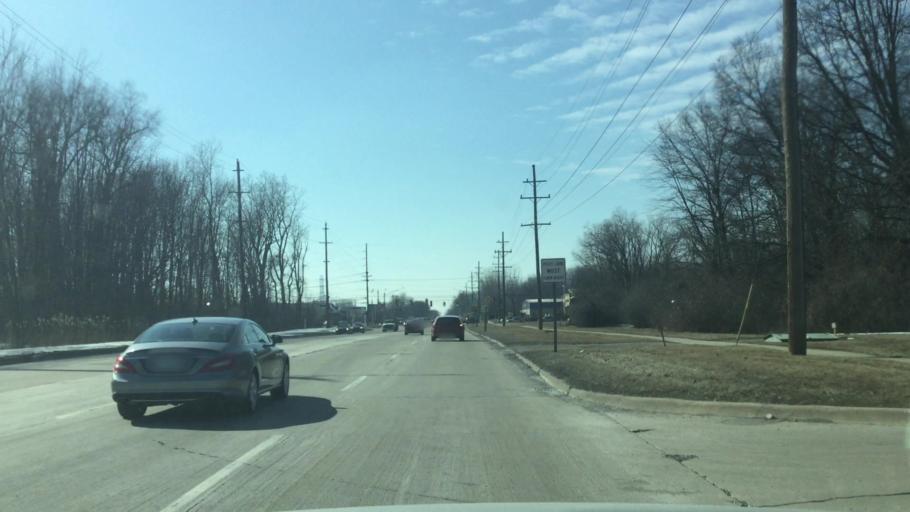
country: US
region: Michigan
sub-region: Wayne County
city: Westland
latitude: 42.3097
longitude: -83.4052
